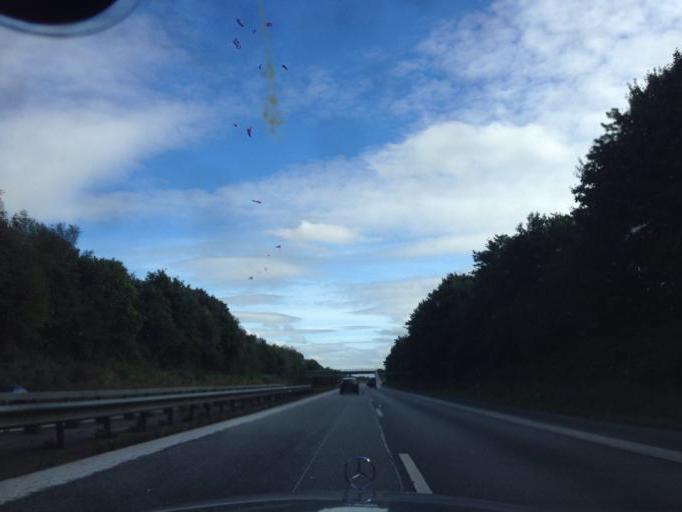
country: DE
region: Schleswig-Holstein
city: Selk
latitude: 54.4726
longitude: 9.5516
